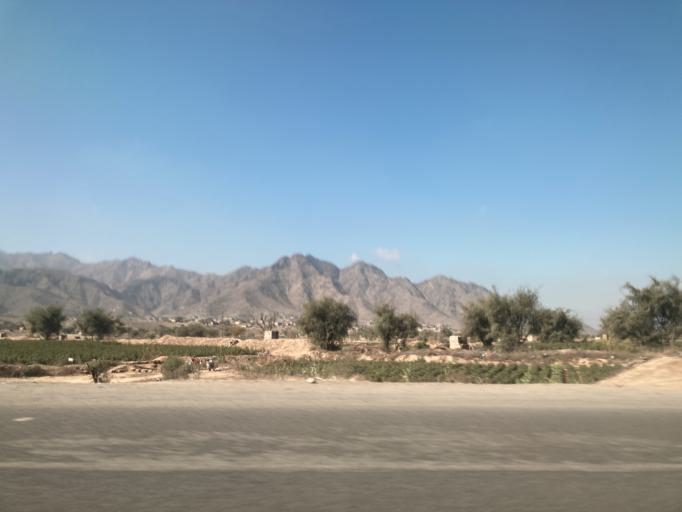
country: YE
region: Ad Dali'
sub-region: Qa'atabah
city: Qa`tabah
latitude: 13.8102
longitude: 44.7222
